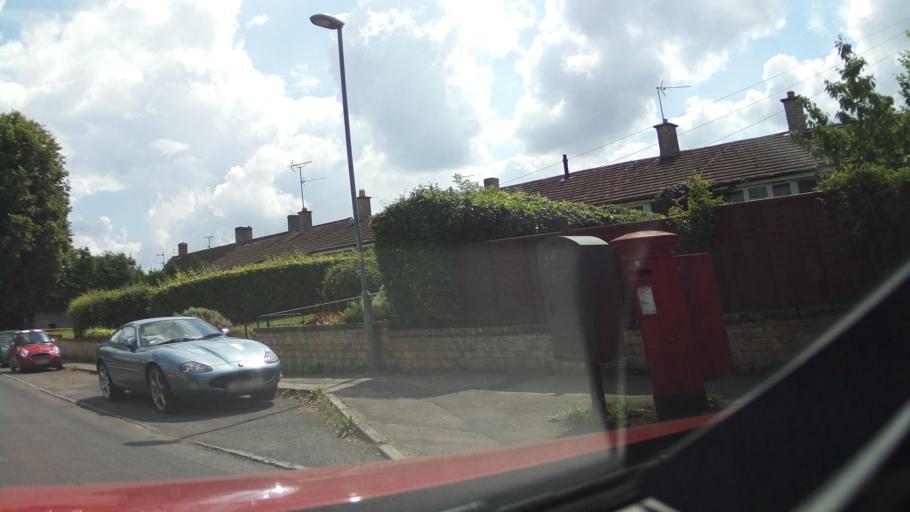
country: GB
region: England
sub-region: Wiltshire
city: Purton
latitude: 51.5863
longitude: -1.8778
